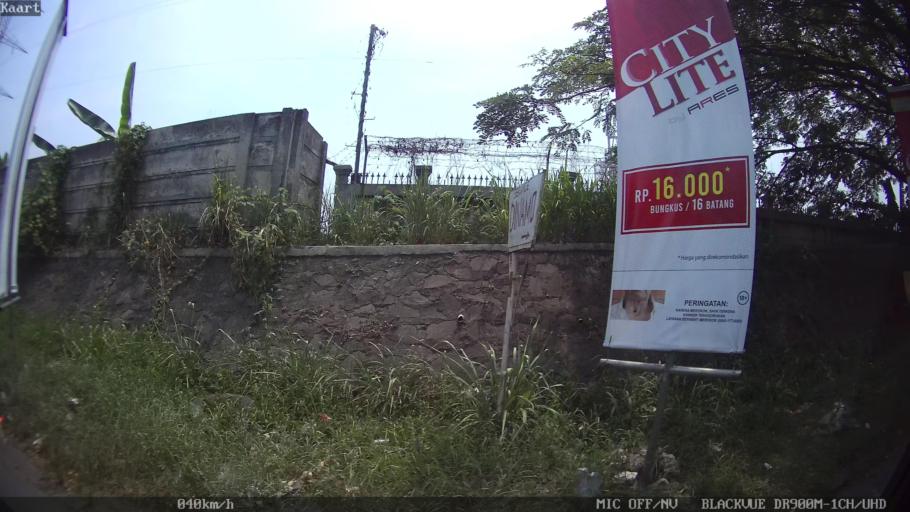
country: ID
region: Banten
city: Curug
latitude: -5.9632
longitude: 106.0060
